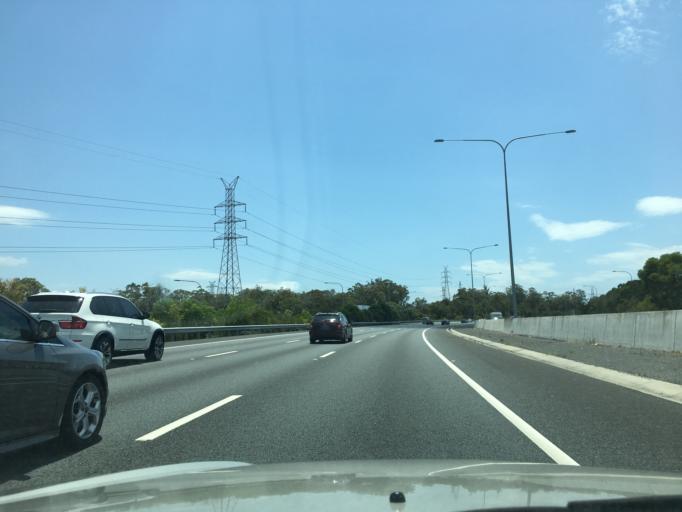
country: AU
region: Queensland
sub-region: Brisbane
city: Mackenzie
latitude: -27.5433
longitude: 153.1171
